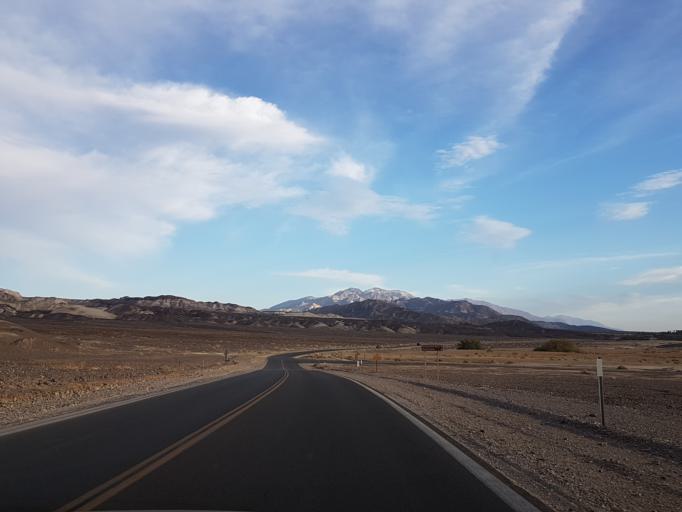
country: US
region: Nevada
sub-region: Nye County
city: Beatty
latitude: 36.4814
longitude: -116.8710
